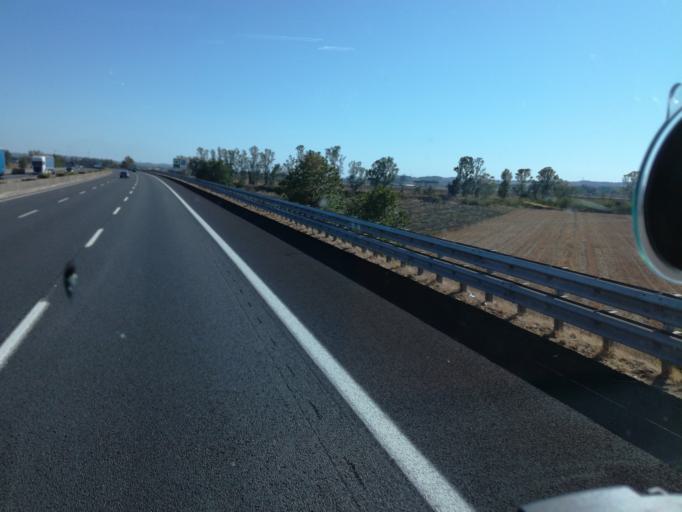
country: IT
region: Latium
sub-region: Citta metropolitana di Roma Capitale
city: Bivio di Capanelle
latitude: 42.1351
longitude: 12.6184
